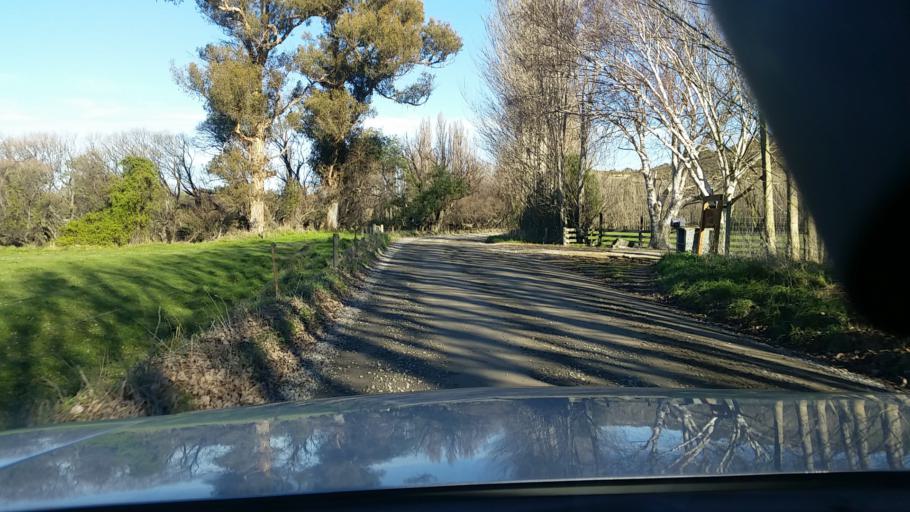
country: NZ
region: Marlborough
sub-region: Marlborough District
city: Blenheim
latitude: -41.4416
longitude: 173.8986
